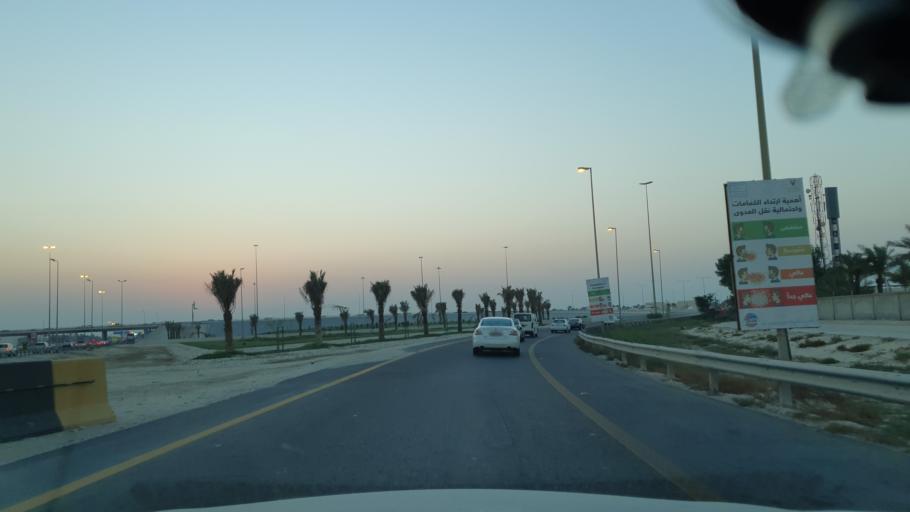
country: BH
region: Central Governorate
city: Madinat Hamad
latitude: 26.1730
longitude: 50.4696
